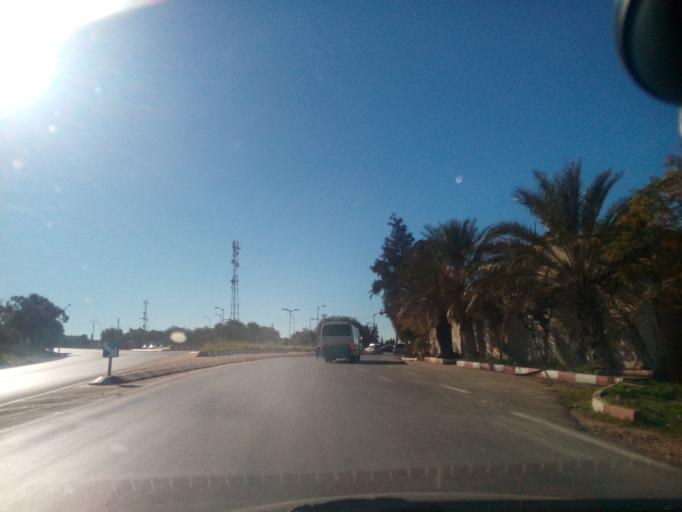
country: DZ
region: Relizane
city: Djidiouia
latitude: 35.8918
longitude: 0.7354
